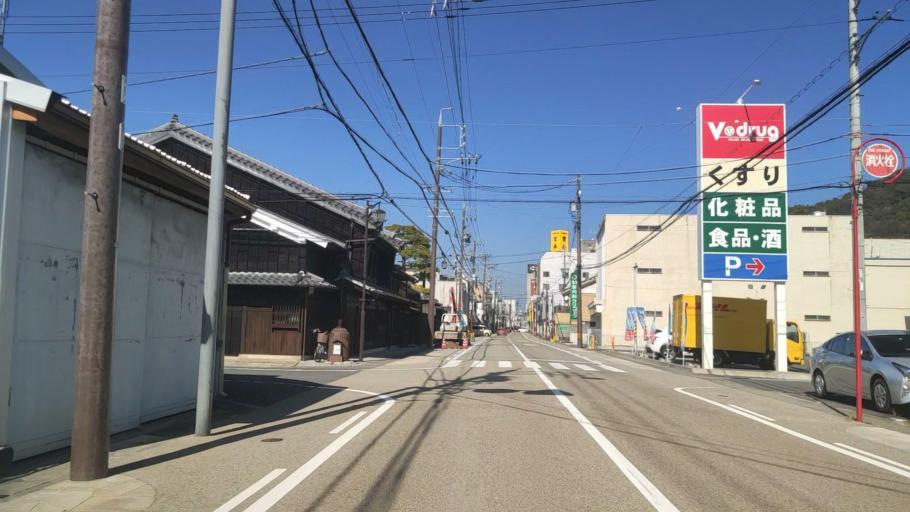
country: JP
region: Gifu
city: Gifu-shi
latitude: 35.4225
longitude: 136.7634
